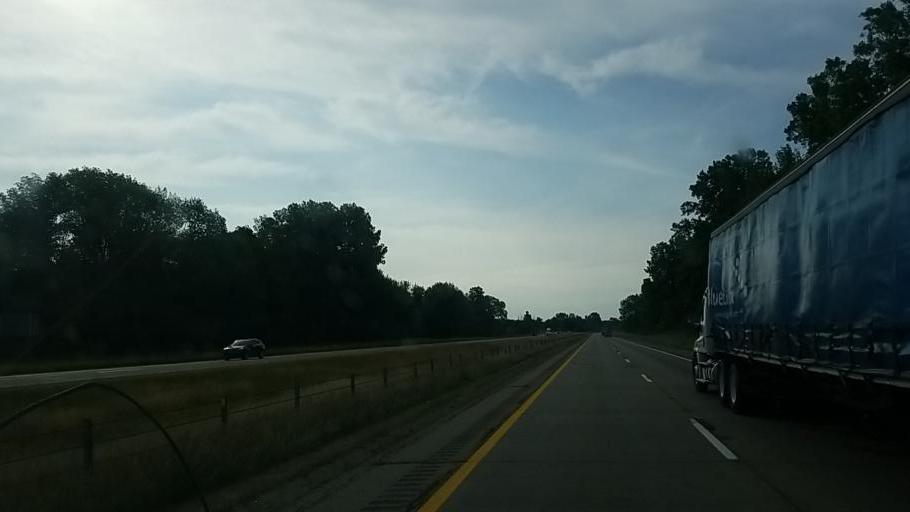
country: US
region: Michigan
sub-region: Ionia County
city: Portland
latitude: 42.8479
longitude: -84.8563
